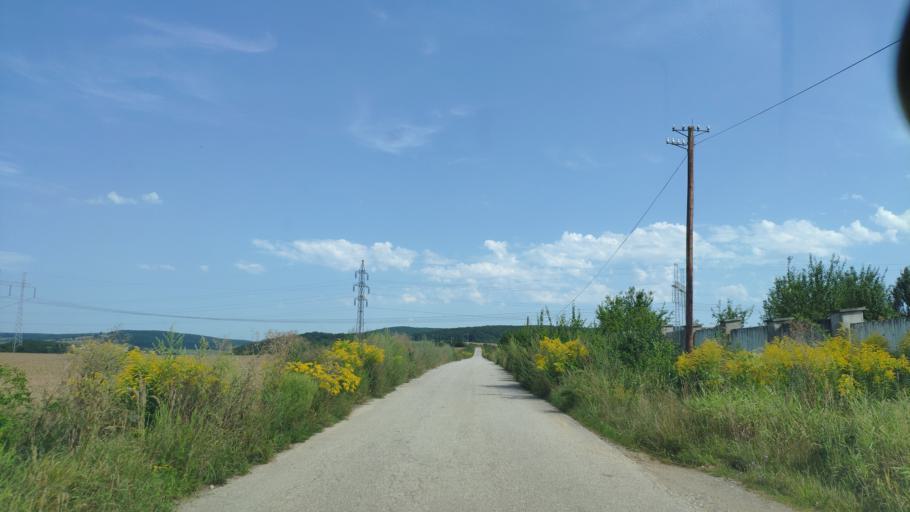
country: HU
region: Borsod-Abauj-Zemplen
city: Putnok
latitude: 48.4431
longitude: 20.3490
